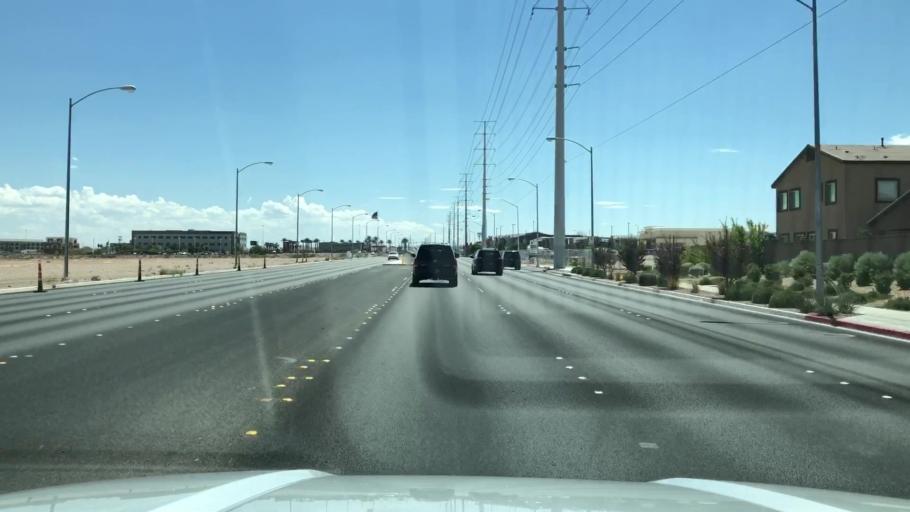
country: US
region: Nevada
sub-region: Clark County
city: Spring Valley
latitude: 36.0765
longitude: -115.2795
